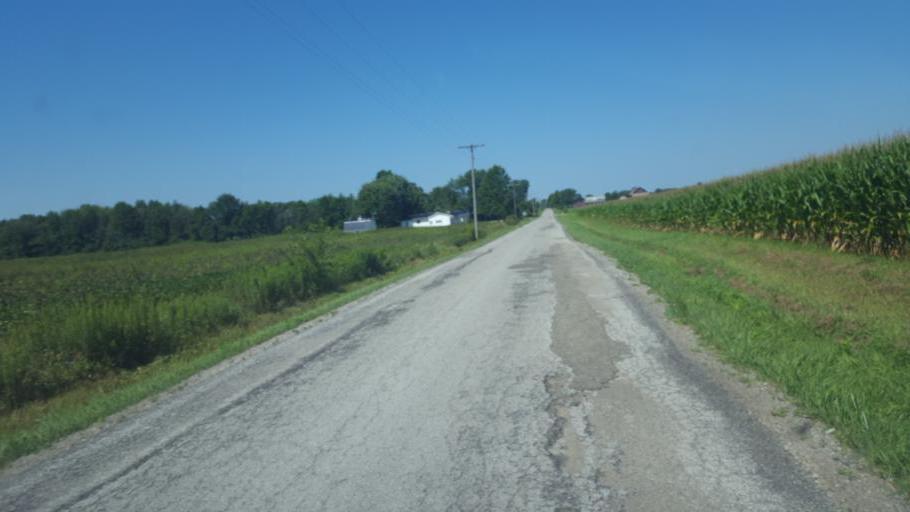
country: US
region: Ohio
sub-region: Delaware County
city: Ashley
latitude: 40.4528
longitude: -82.9280
